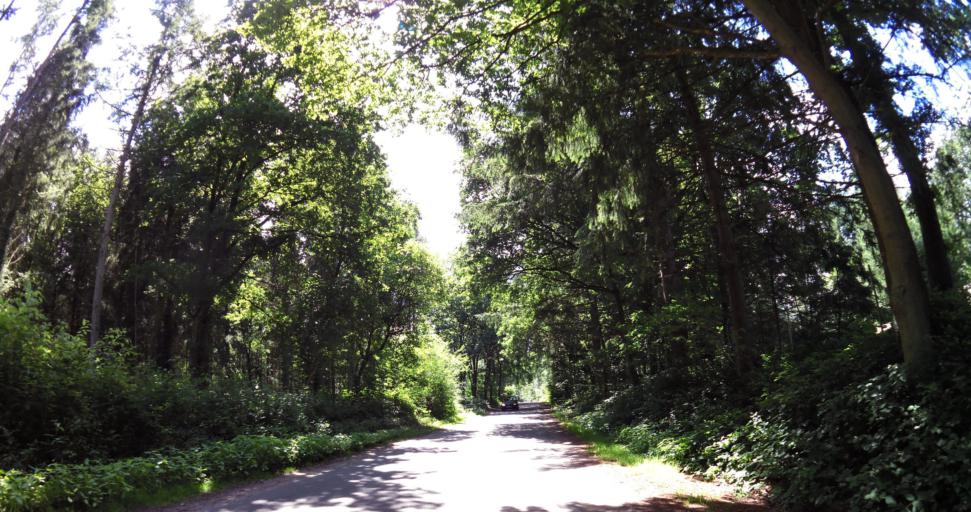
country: DE
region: Schleswig-Holstein
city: Brodersby
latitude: 54.5161
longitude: 9.7207
